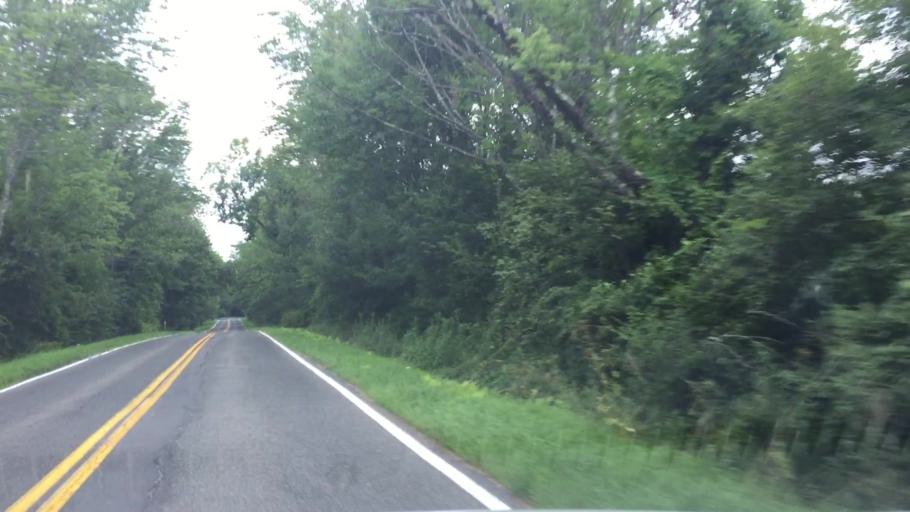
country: US
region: Massachusetts
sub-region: Berkshire County
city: Housatonic
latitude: 42.2783
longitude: -73.4079
